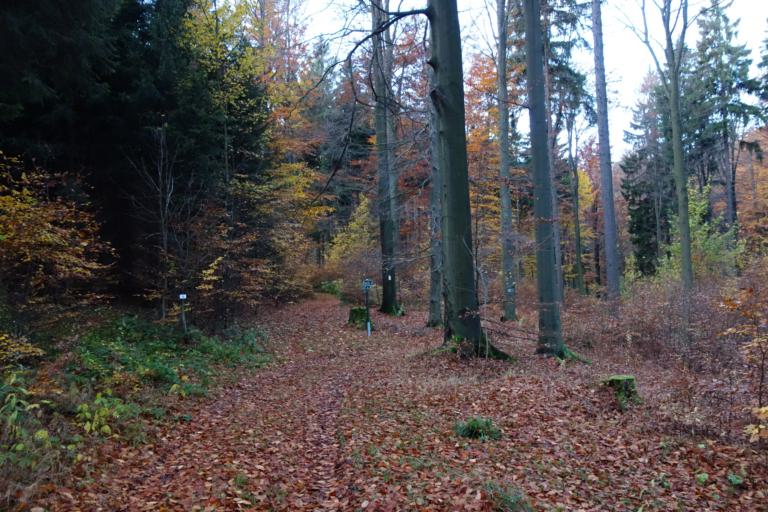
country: DE
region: Saxony
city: Rechenberg-Bienenmuhle
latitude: 50.7317
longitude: 13.5341
